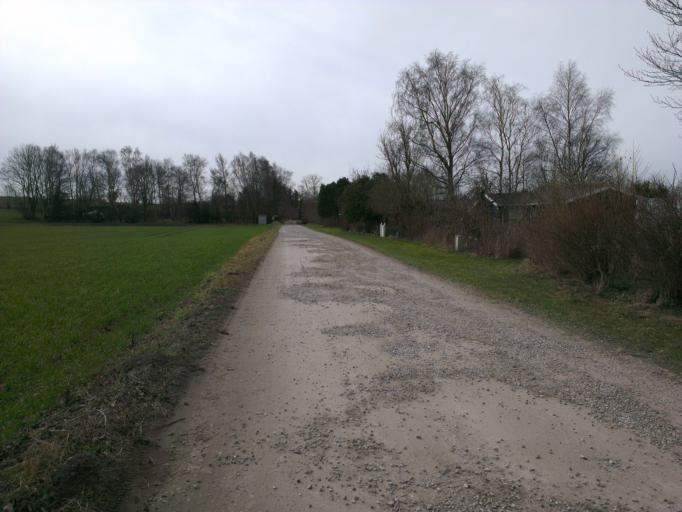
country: DK
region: Zealand
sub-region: Lejre Kommune
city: Ejby
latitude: 55.7871
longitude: 11.8657
